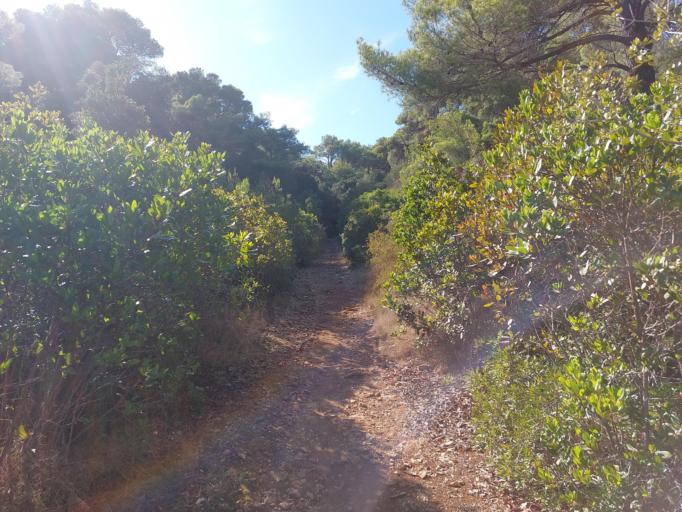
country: HR
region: Dubrovacko-Neretvanska
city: Smokvica
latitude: 42.7643
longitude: 16.8067
